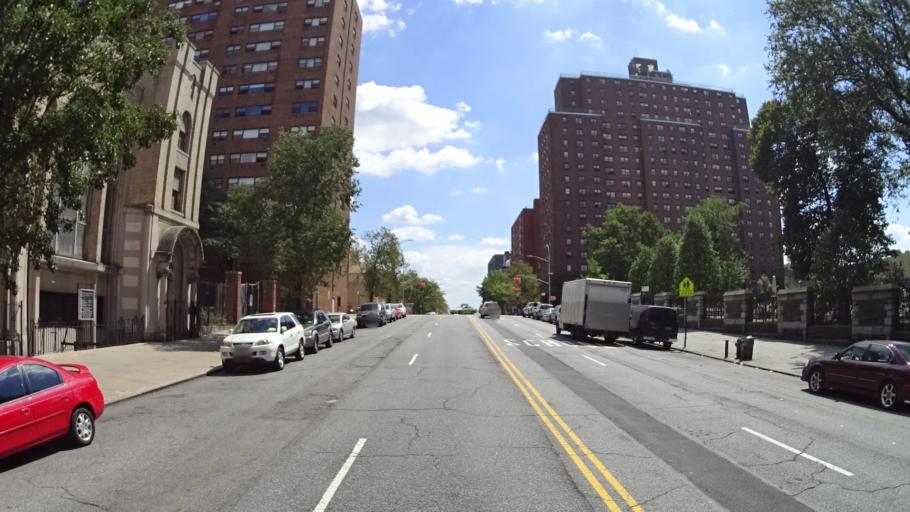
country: US
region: New Jersey
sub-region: Bergen County
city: Edgewater
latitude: 40.8320
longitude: -73.9438
